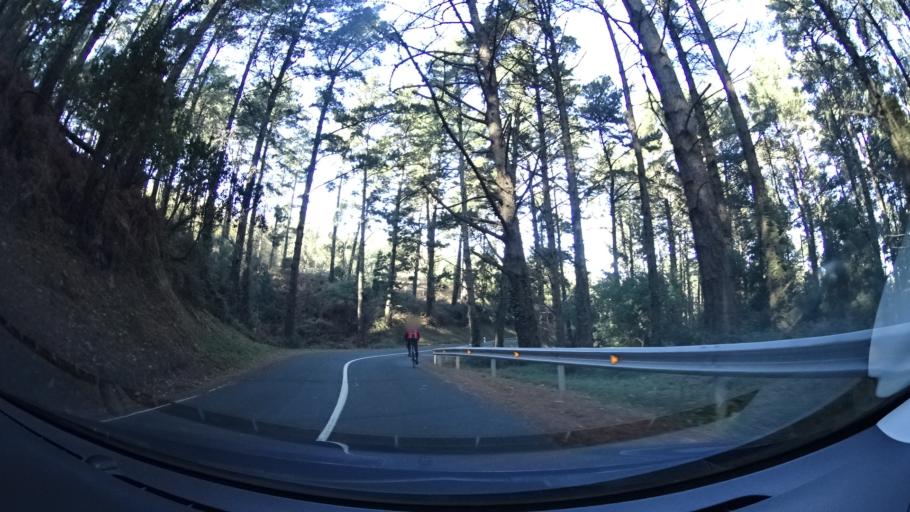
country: ES
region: Basque Country
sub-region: Bizkaia
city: Bermeo
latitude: 43.4404
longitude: -2.7530
